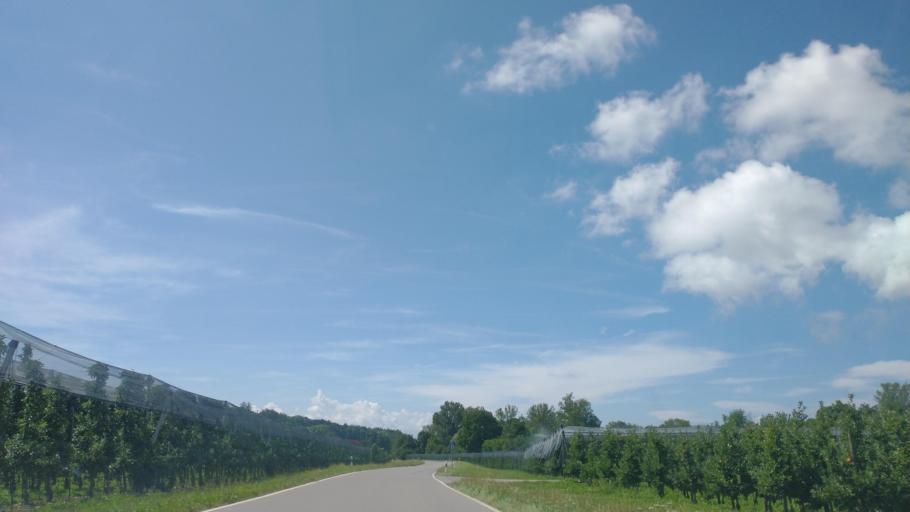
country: DE
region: Baden-Wuerttemberg
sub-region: Tuebingen Region
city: Kressbronn am Bodensee
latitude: 47.6271
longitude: 9.5972
